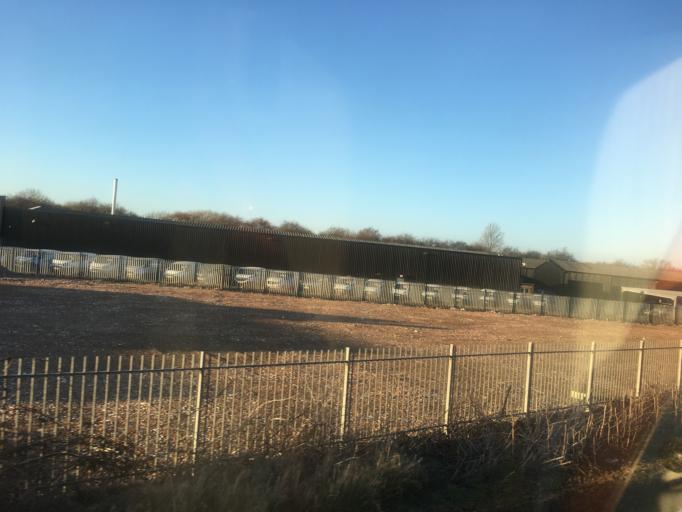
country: GB
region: England
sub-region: Derbyshire
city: Long Eaton
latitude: 52.8923
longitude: -1.2546
